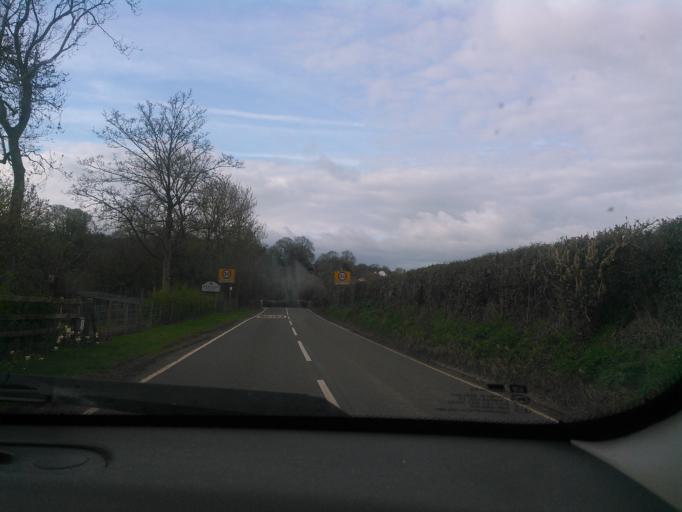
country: GB
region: England
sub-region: Shropshire
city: Bayston Hill
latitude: 52.6800
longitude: -2.7890
